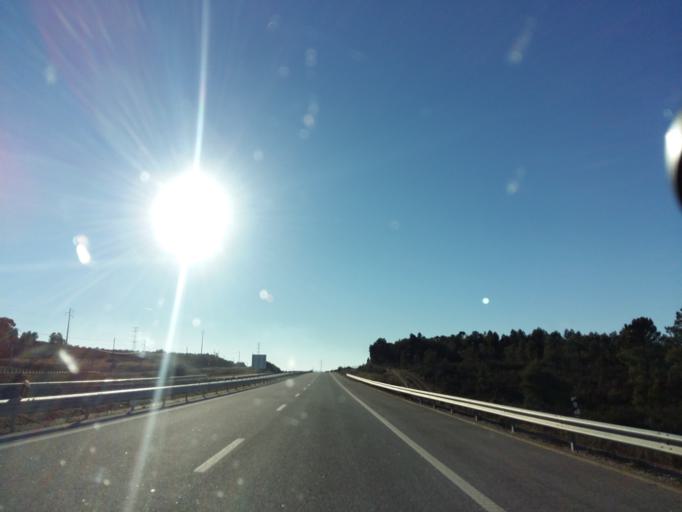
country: PT
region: Castelo Branco
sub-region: Castelo Branco
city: Castelo Branco
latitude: 39.7813
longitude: -7.5786
